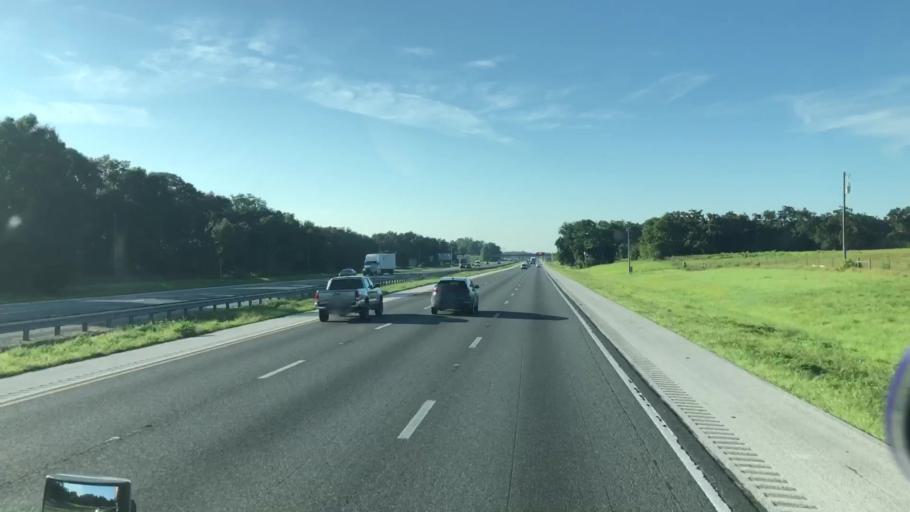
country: US
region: Florida
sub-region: Sumter County
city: Wildwood
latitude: 28.9016
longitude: -82.1047
